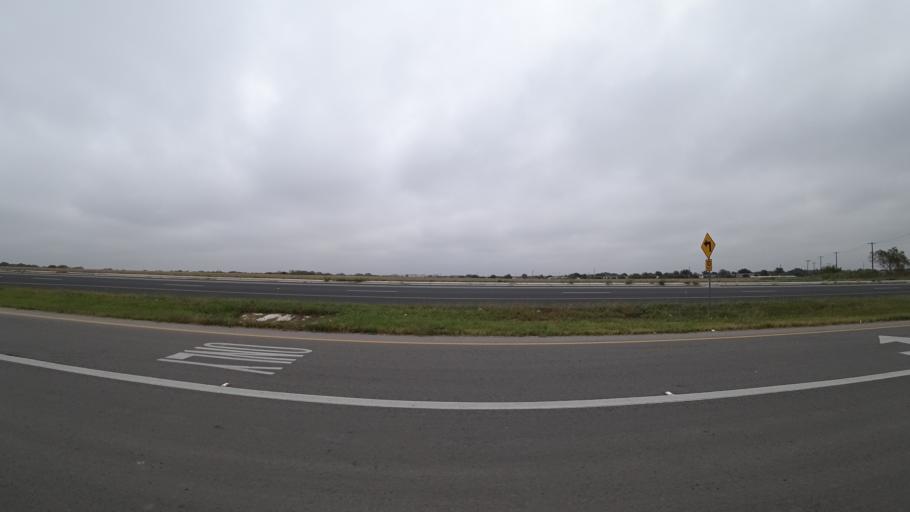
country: US
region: Texas
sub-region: Travis County
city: Pflugerville
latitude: 30.4161
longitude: -97.6124
